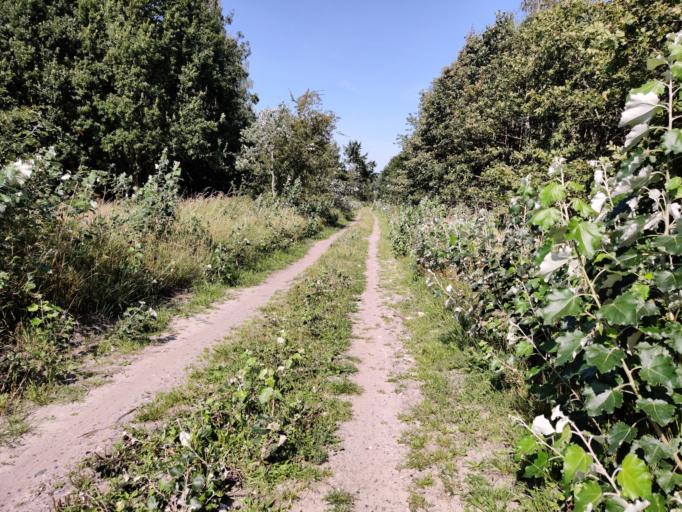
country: DK
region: Zealand
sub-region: Guldborgsund Kommune
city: Nykobing Falster
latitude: 54.6182
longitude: 11.9563
